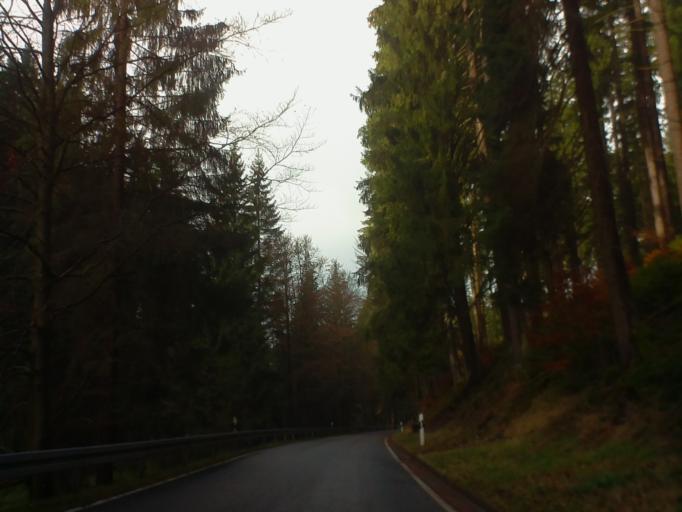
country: DE
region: Thuringia
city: Altenfeld
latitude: 50.5390
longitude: 10.9660
